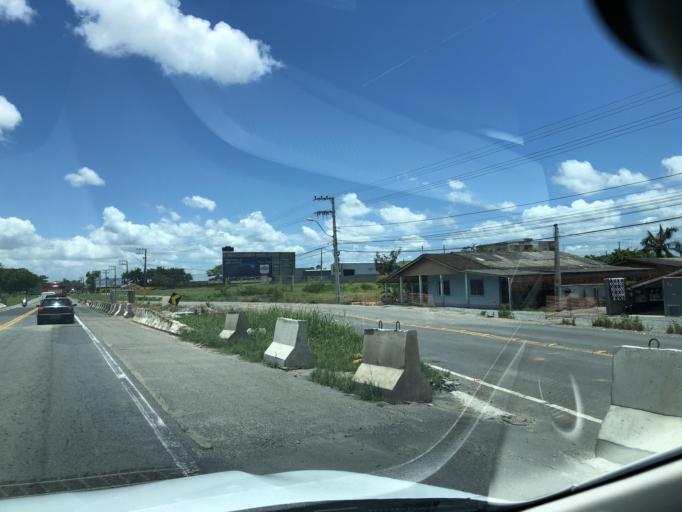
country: BR
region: Santa Catarina
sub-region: Joinville
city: Joinville
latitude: -26.4014
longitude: -48.7433
